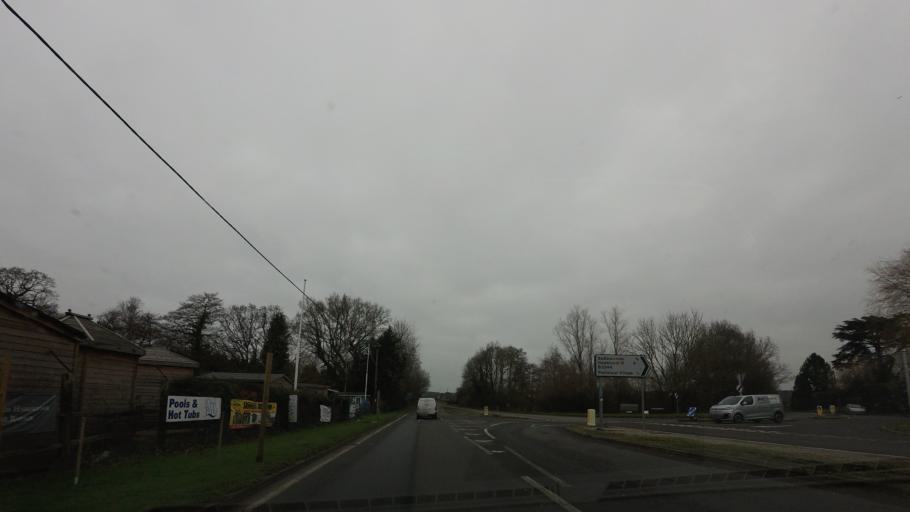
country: GB
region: England
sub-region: East Sussex
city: Battle
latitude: 50.9246
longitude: 0.5330
